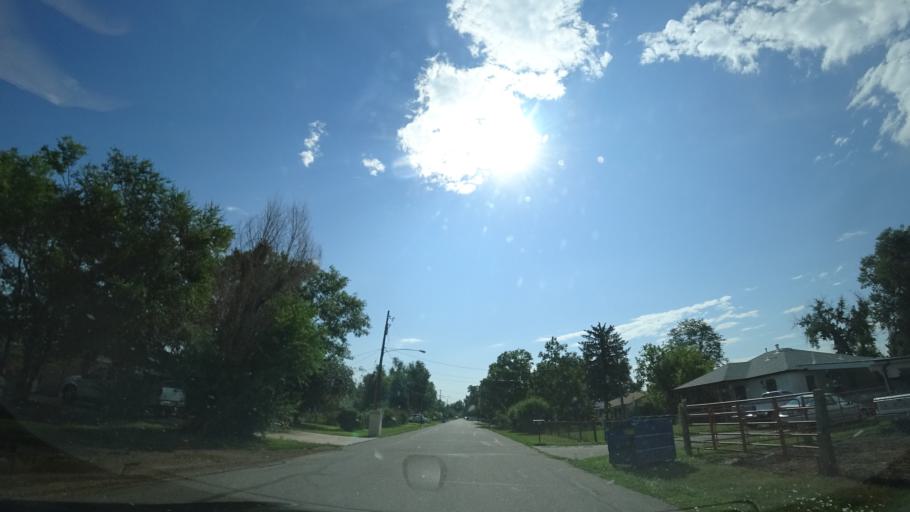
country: US
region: Colorado
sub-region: Jefferson County
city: Lakewood
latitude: 39.7211
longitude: -105.0608
